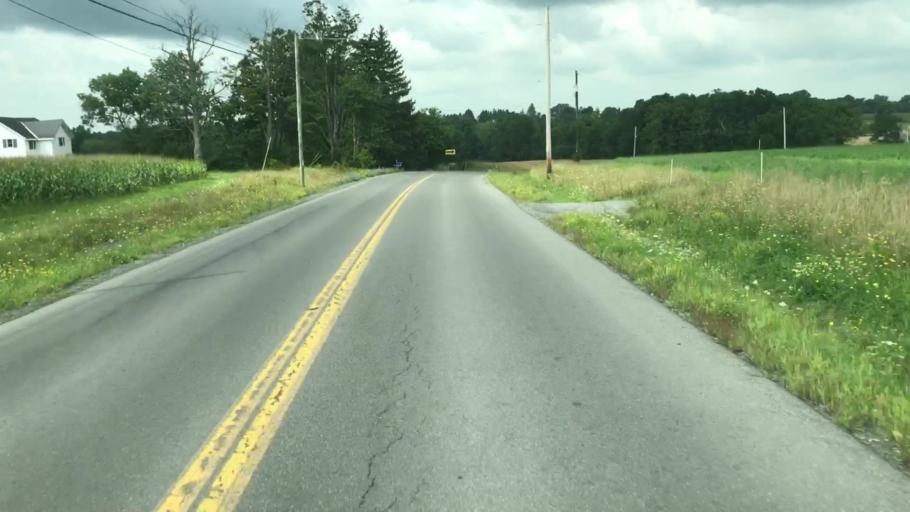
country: US
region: New York
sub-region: Cayuga County
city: Melrose Park
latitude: 42.9171
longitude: -76.5185
